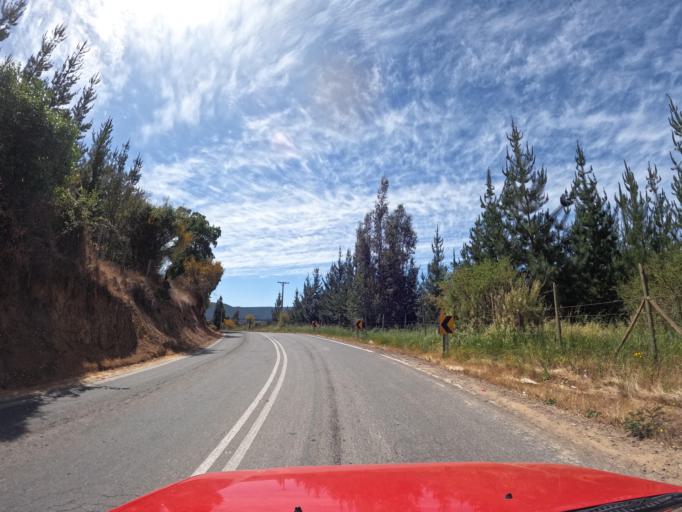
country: CL
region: Maule
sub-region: Provincia de Talca
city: Talca
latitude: -34.9913
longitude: -71.8104
